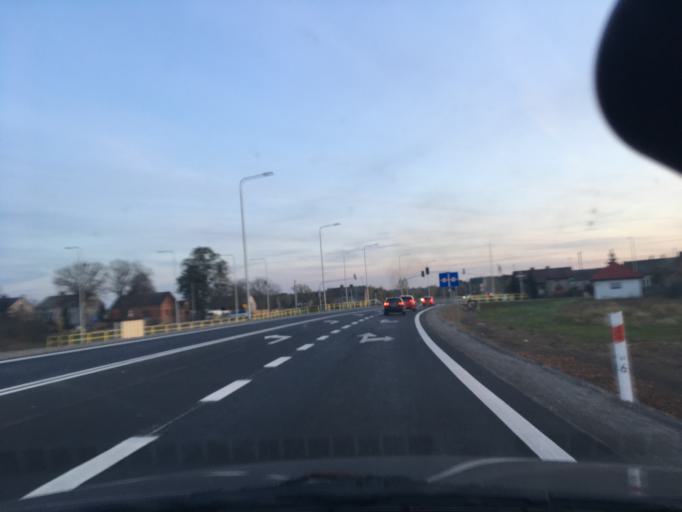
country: PL
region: Masovian Voivodeship
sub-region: Powiat plocki
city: Wyszogrod
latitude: 52.3577
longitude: 20.2079
